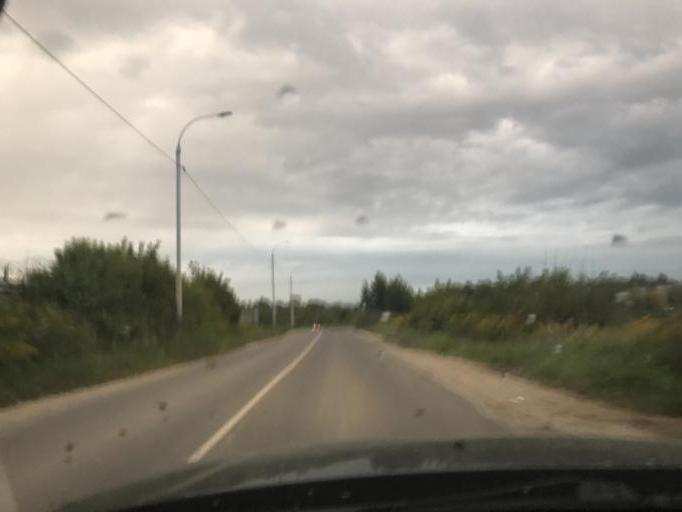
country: RU
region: Tula
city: Gorelki
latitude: 54.2244
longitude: 37.5935
